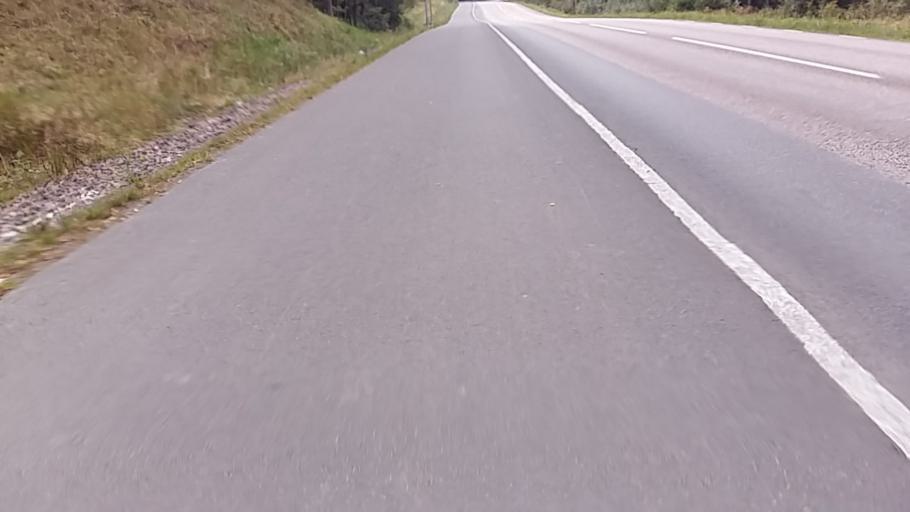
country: SE
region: Joenkoeping
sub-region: Jonkopings Kommun
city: Odensjo
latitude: 57.7196
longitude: 14.1328
